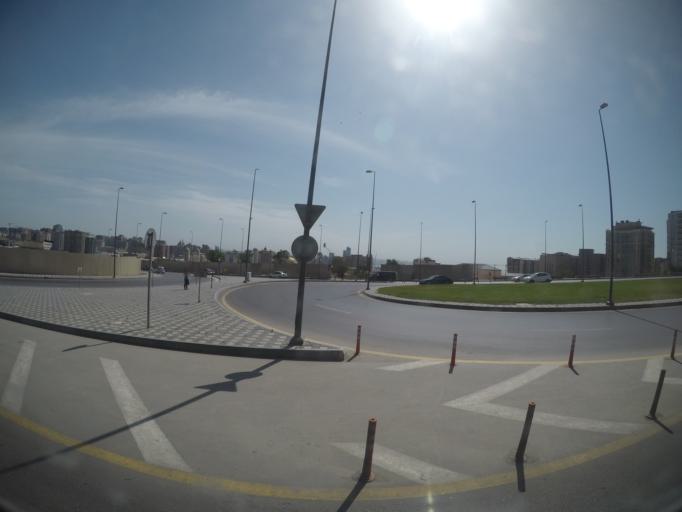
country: AZ
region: Baki
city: Badamdar
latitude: 40.3712
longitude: 49.8246
